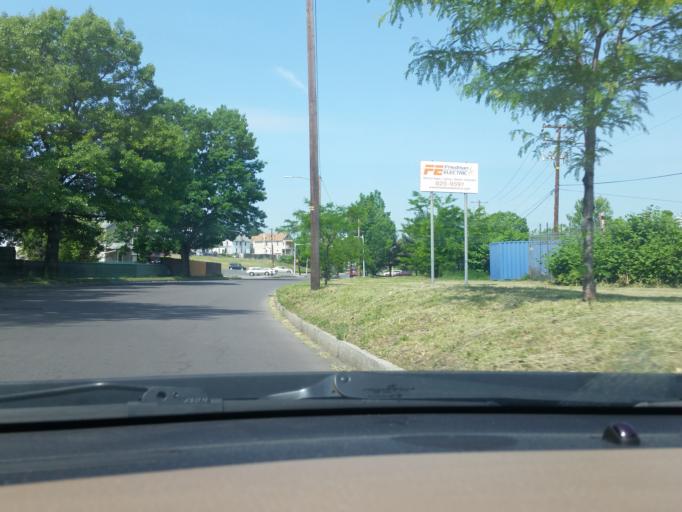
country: US
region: Pennsylvania
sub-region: Luzerne County
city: Wilkes-Barre
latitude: 41.2366
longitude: -75.8886
